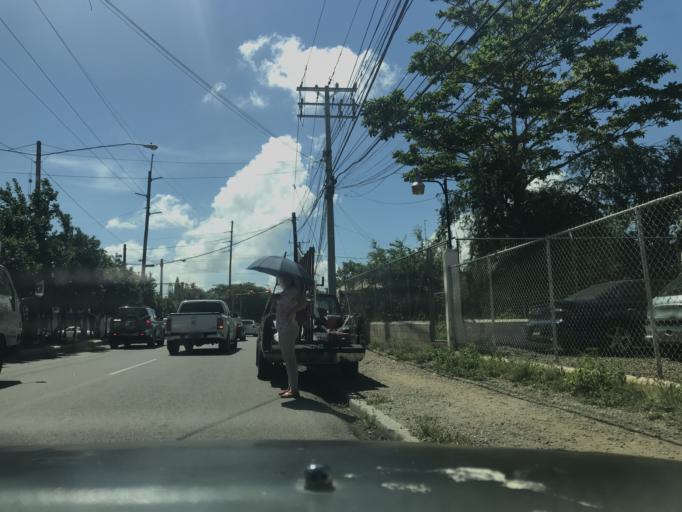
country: DO
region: Santiago
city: Santiago de los Caballeros
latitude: 19.4399
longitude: -70.7232
